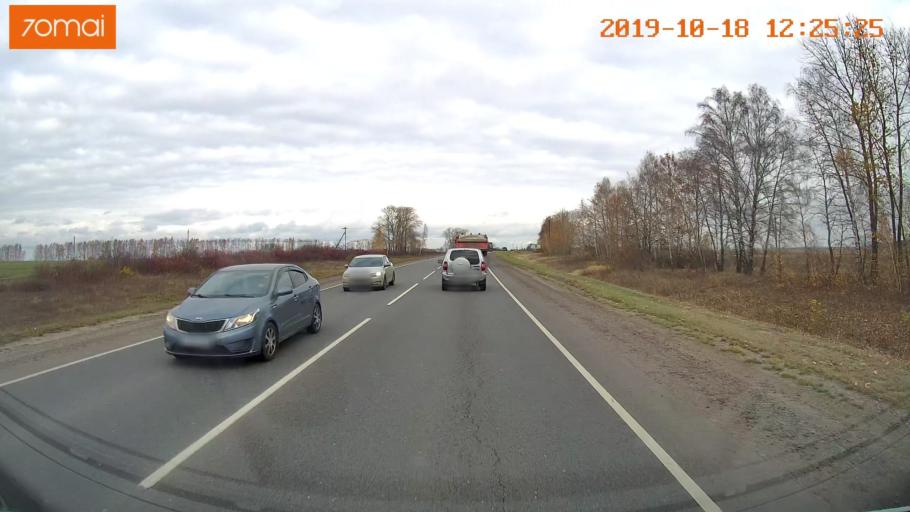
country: RU
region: Rjazan
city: Rybnoye
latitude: 54.5498
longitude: 39.5204
